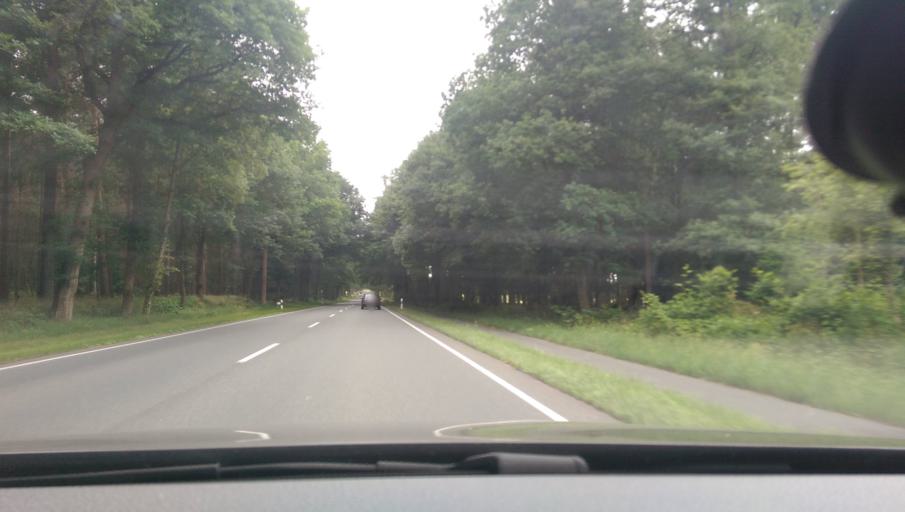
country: DE
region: Lower Saxony
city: Kirchlinteln
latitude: 52.9925
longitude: 9.2659
